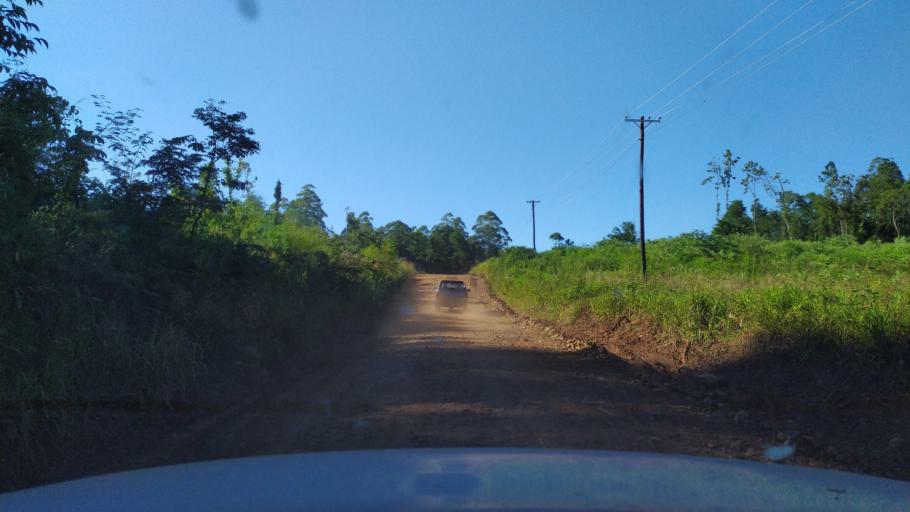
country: AR
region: Misiones
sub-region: Departamento de Montecarlo
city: Montecarlo
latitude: -26.6196
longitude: -54.6964
